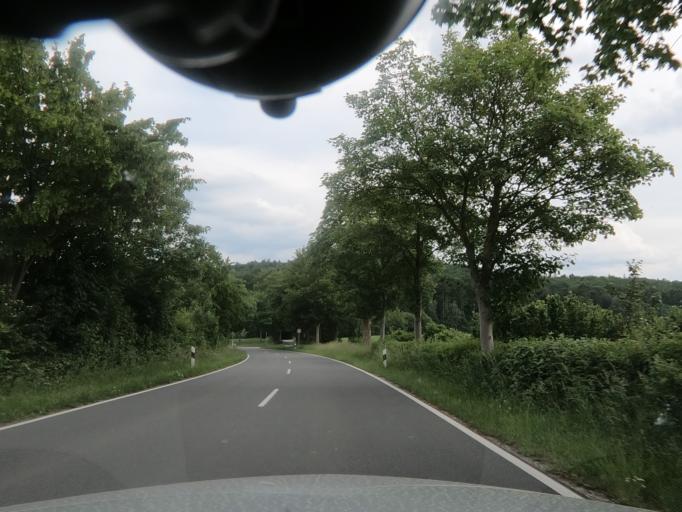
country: DE
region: North Rhine-Westphalia
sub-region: Regierungsbezirk Arnsberg
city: Ruthen
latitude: 51.4425
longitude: 8.4284
